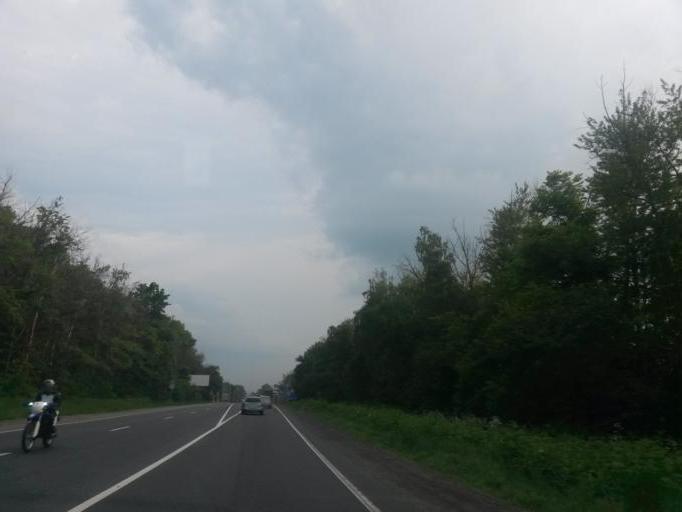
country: RU
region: Moskovskaya
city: Gorki-Leninskiye
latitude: 55.5206
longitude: 37.7624
